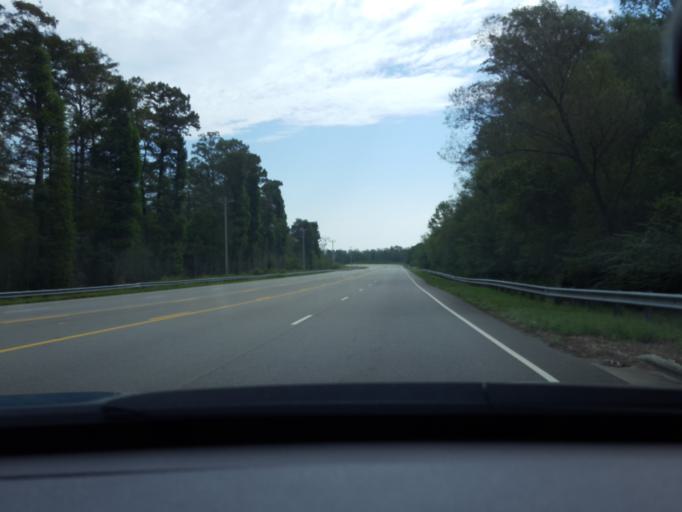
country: US
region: North Carolina
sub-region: Chowan County
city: Edenton
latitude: 36.0377
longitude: -76.7670
